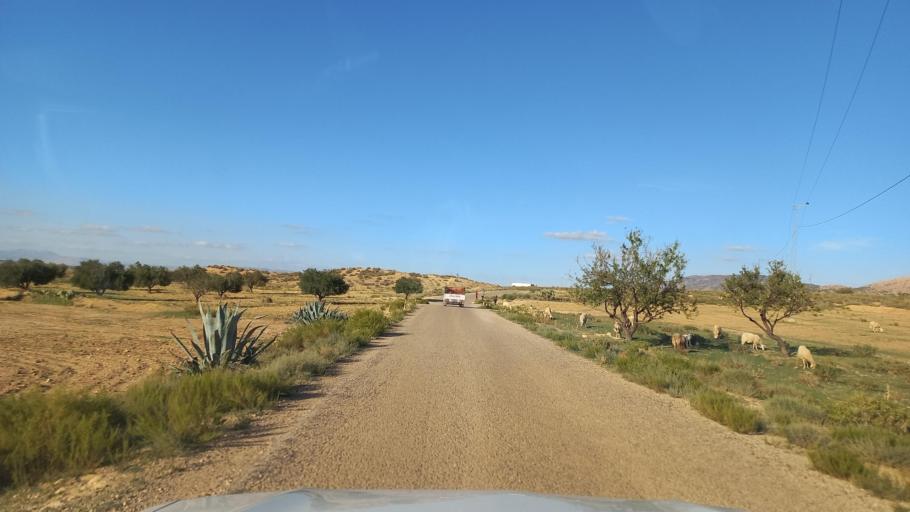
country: TN
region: Al Qasrayn
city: Sbiba
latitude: 35.3522
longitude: 9.1351
